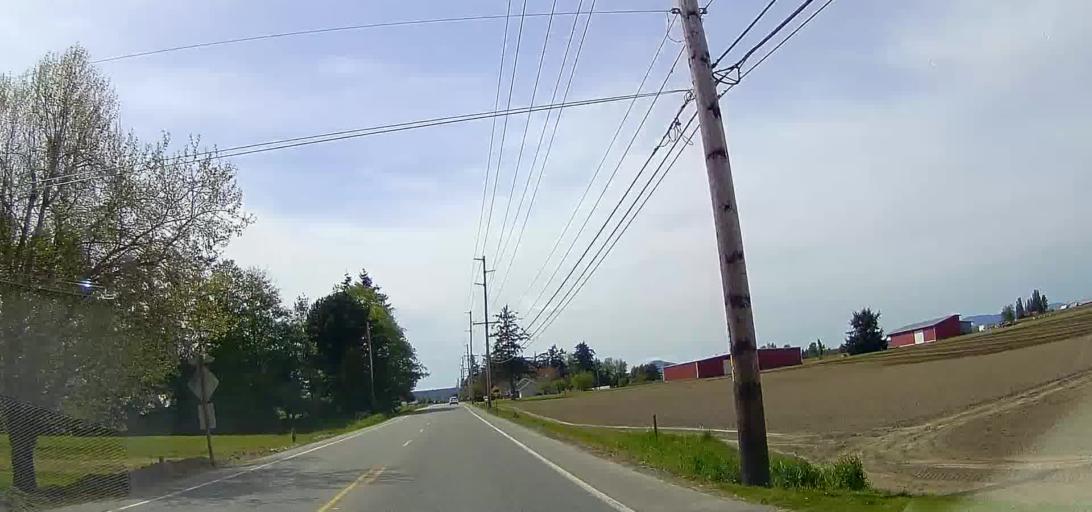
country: US
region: Washington
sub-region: Skagit County
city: Mount Vernon
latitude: 48.4209
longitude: -122.4245
